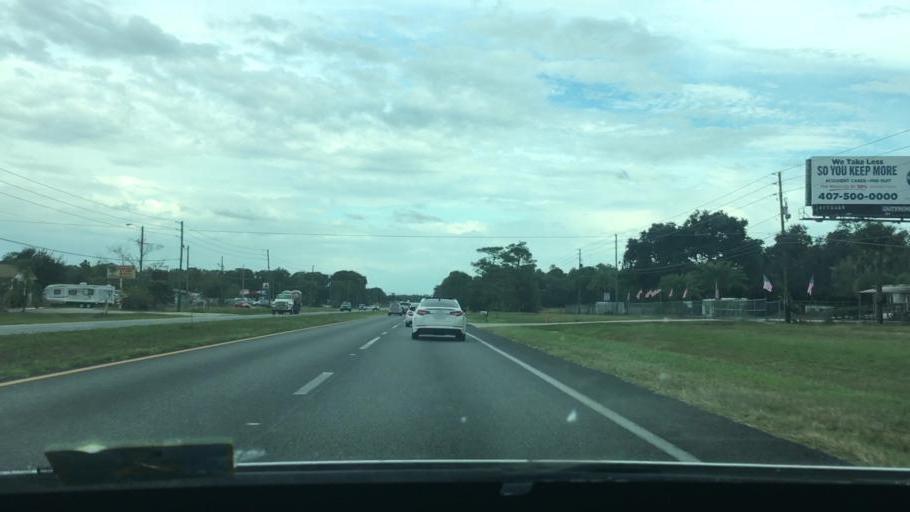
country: US
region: Florida
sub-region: Orange County
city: Bithlo
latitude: 28.5560
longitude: -81.1147
